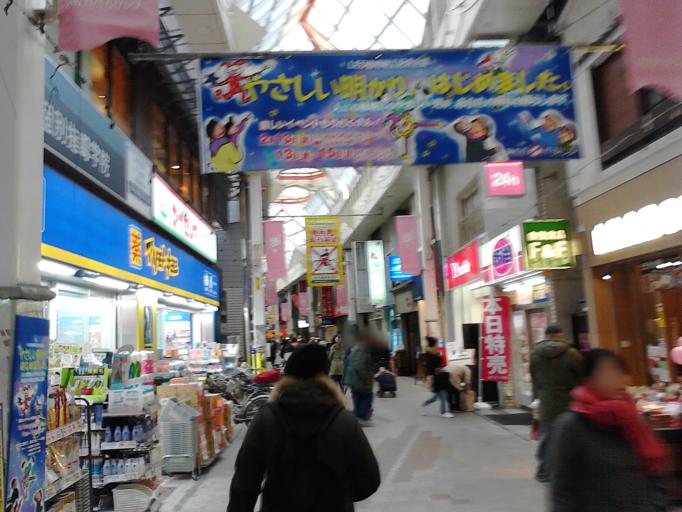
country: JP
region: Tokyo
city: Tokyo
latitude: 35.7026
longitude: 139.6366
